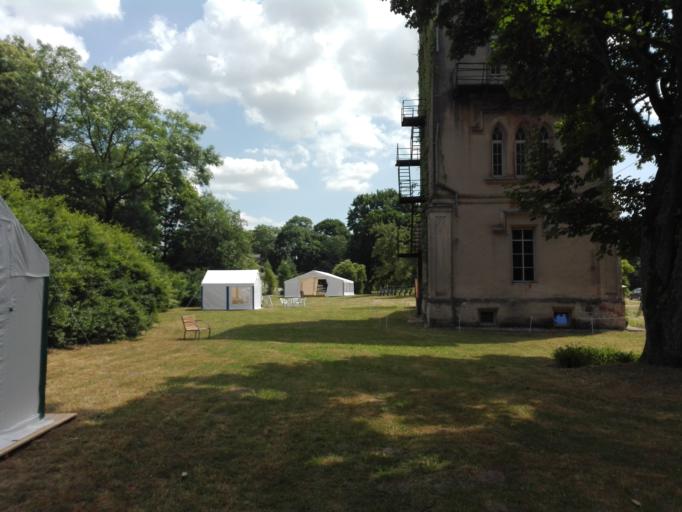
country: LT
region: Vilnius County
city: Ukmerge
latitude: 55.2097
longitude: 24.7978
